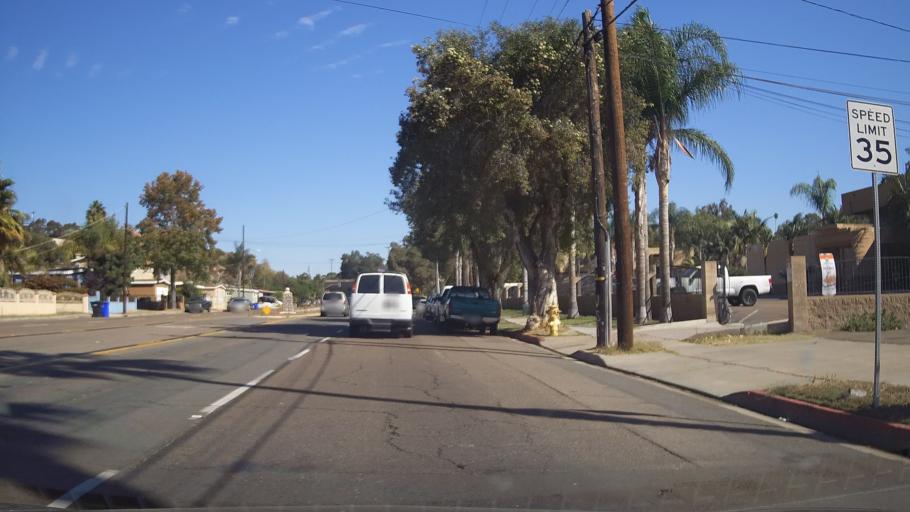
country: US
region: California
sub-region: San Diego County
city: National City
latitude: 32.7238
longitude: -117.1064
